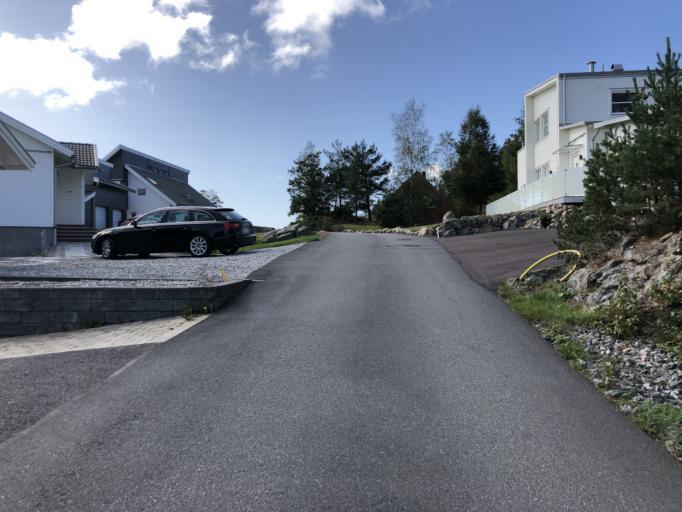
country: SE
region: Vaestra Goetaland
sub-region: Goteborg
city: Torslanda
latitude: 57.7490
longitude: 11.8226
